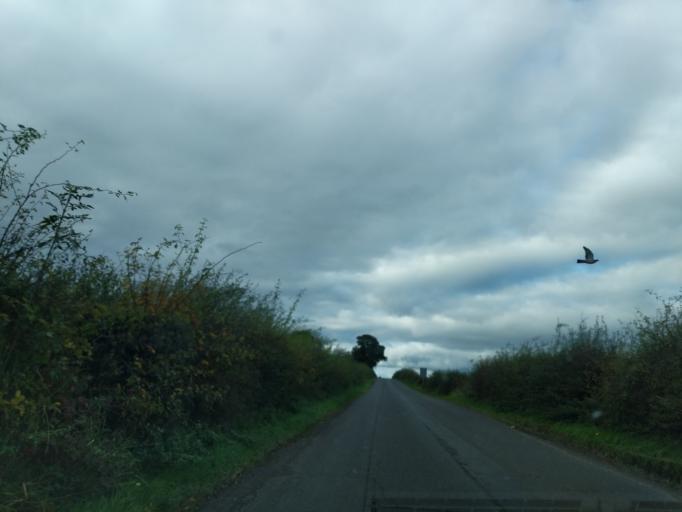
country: GB
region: Scotland
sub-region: East Lothian
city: Haddington
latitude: 55.9299
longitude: -2.8287
